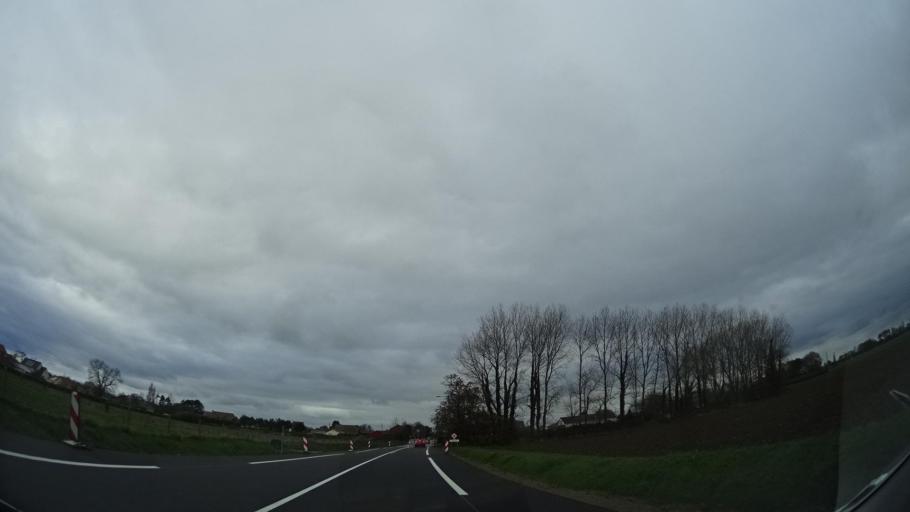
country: FR
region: Haute-Normandie
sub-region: Departement de la Seine-Maritime
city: Octeville-sur-Mer
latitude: 49.5758
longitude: 0.1201
